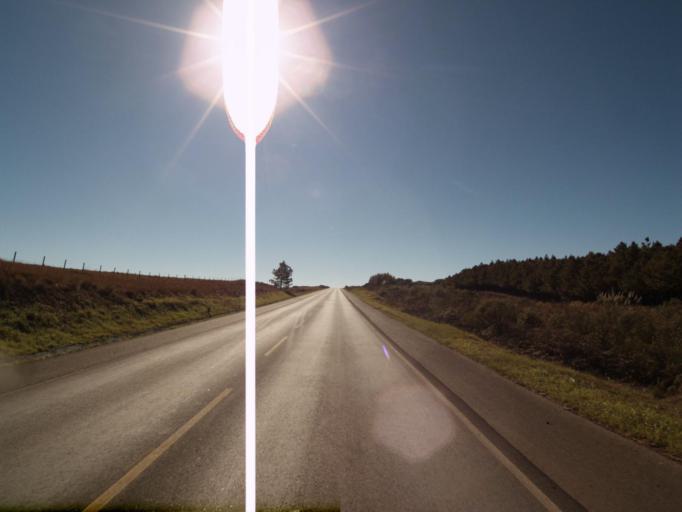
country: BR
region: Parana
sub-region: Palmas
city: Palmas
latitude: -26.7397
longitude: -51.6525
